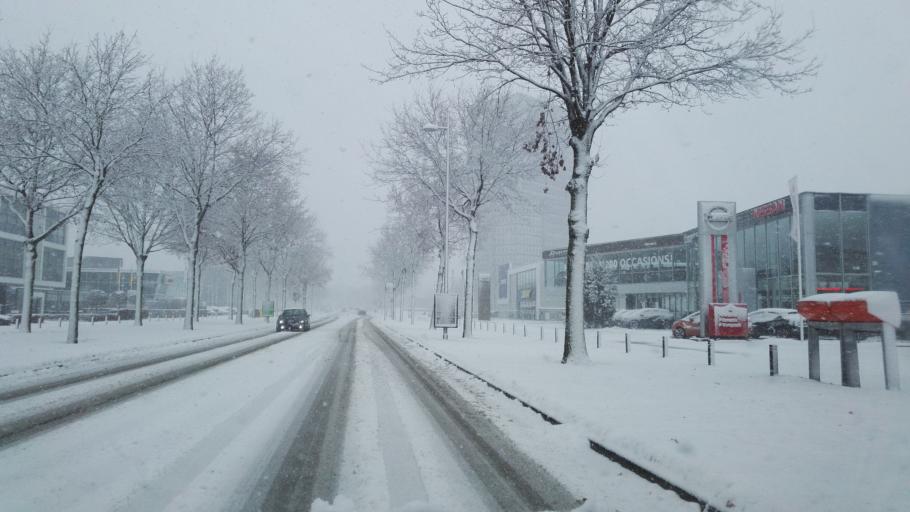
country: NL
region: Gelderland
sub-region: Gemeente Apeldoorn
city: Apeldoorn
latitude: 52.2380
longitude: 5.9834
